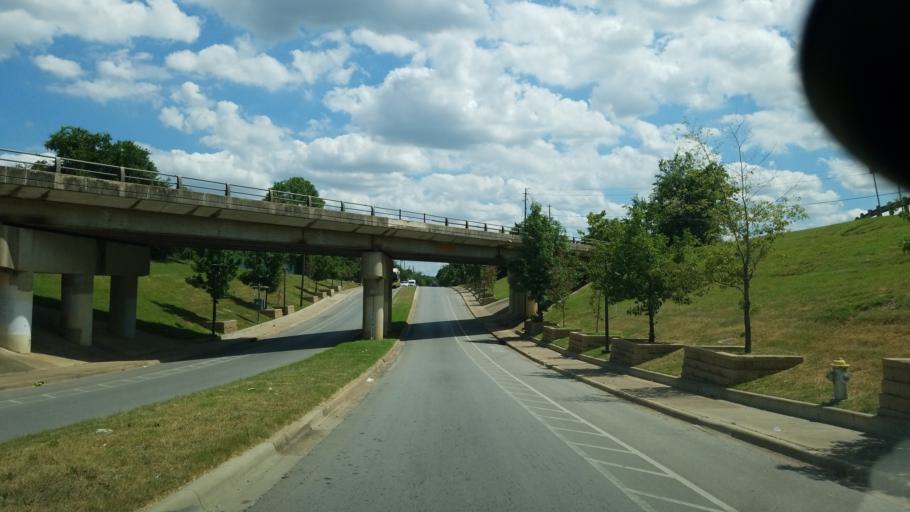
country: US
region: Texas
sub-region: Dallas County
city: Dallas
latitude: 32.7441
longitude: -96.7534
